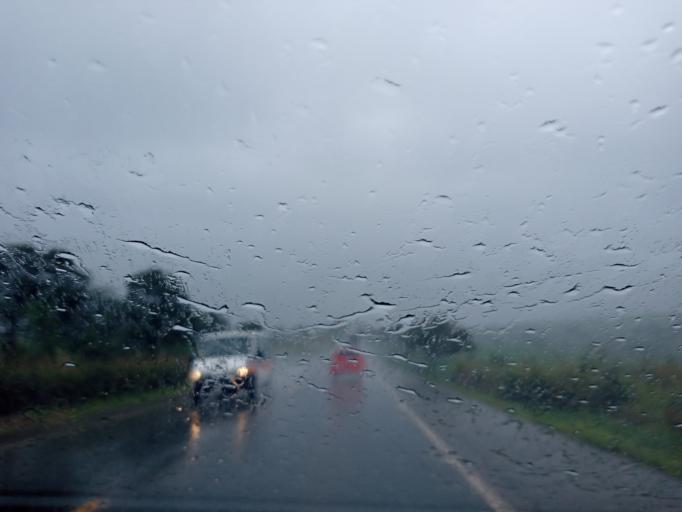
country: BR
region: Minas Gerais
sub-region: Luz
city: Luz
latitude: -19.7801
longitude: -45.7349
